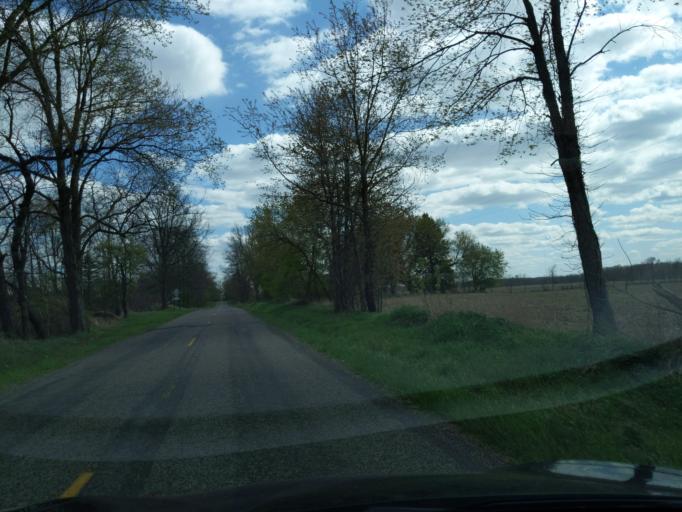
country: US
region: Michigan
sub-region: Ingham County
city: Leslie
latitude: 42.4792
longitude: -84.5412
